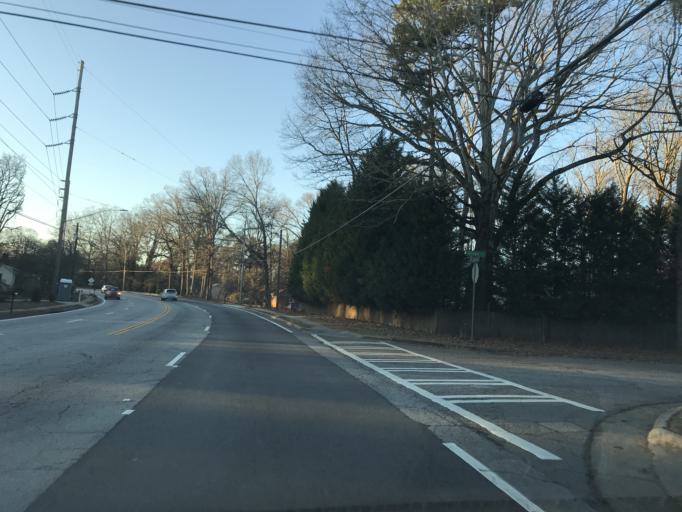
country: US
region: Georgia
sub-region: DeKalb County
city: Tucker
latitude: 33.8610
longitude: -84.2193
